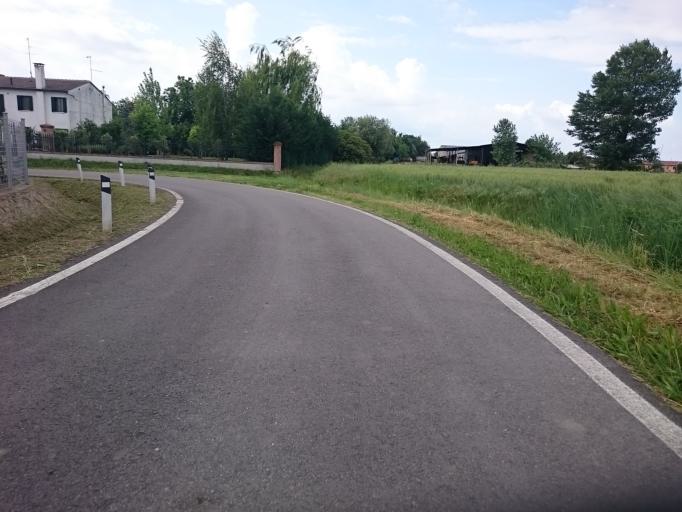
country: IT
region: Veneto
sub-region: Provincia di Padova
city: Megliadino San Vitale
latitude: 45.2009
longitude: 11.5398
